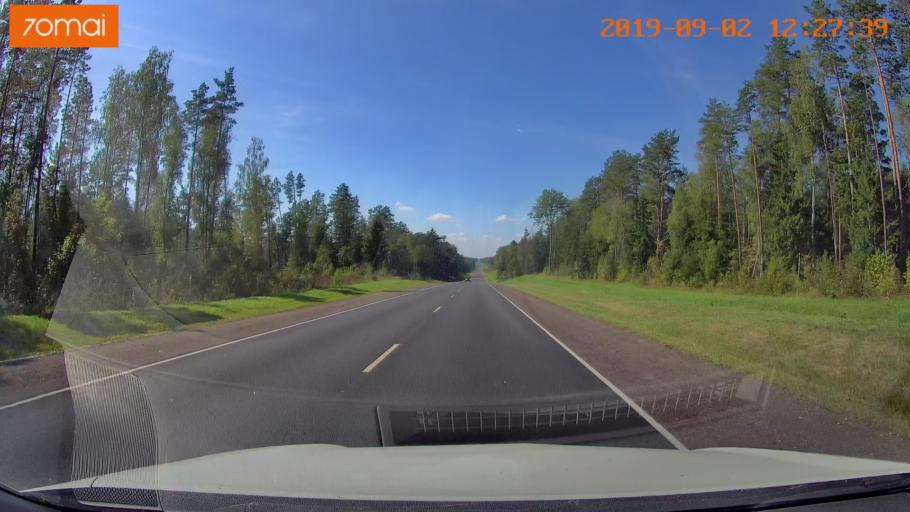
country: RU
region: Smolensk
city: Shumyachi
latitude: 53.8519
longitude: 32.5387
